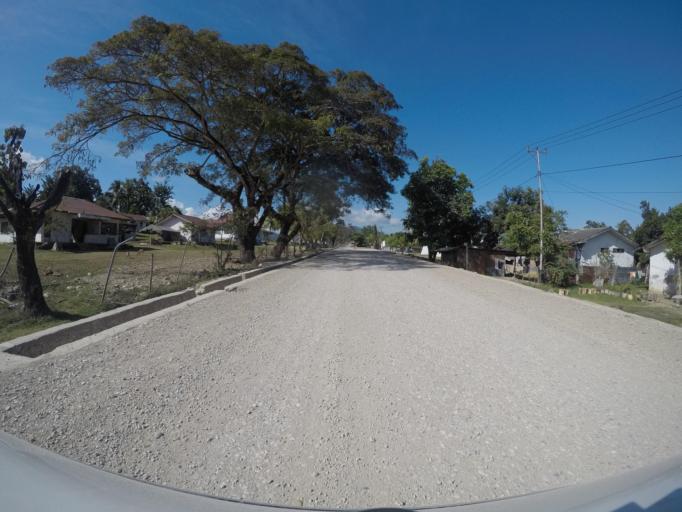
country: TL
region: Viqueque
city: Viqueque
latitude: -8.8224
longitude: 126.5322
